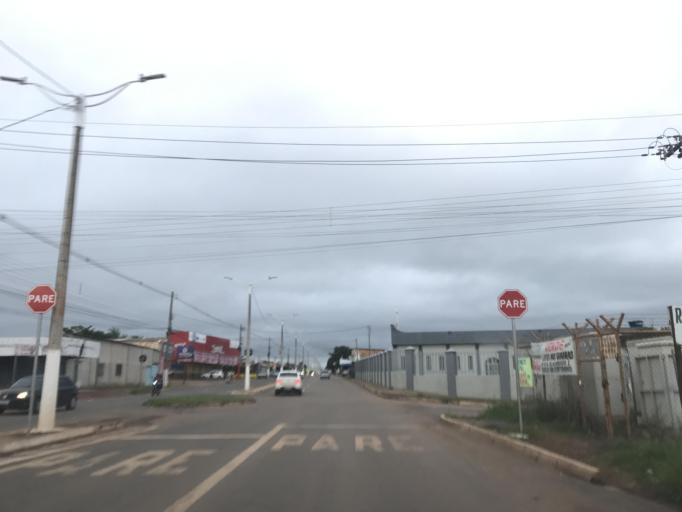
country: BR
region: Goias
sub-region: Luziania
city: Luziania
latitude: -16.2114
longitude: -47.9287
